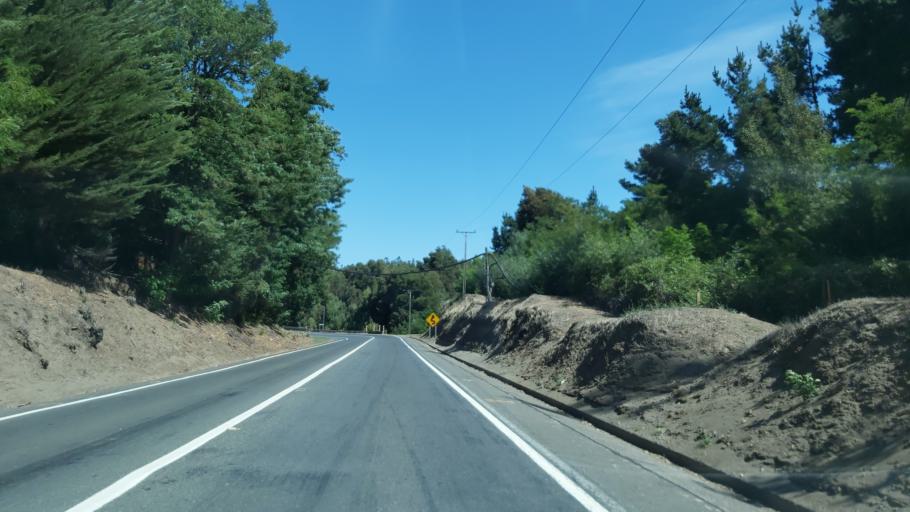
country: CL
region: Biobio
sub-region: Provincia de Concepcion
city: Coronel
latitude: -37.1103
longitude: -72.9878
